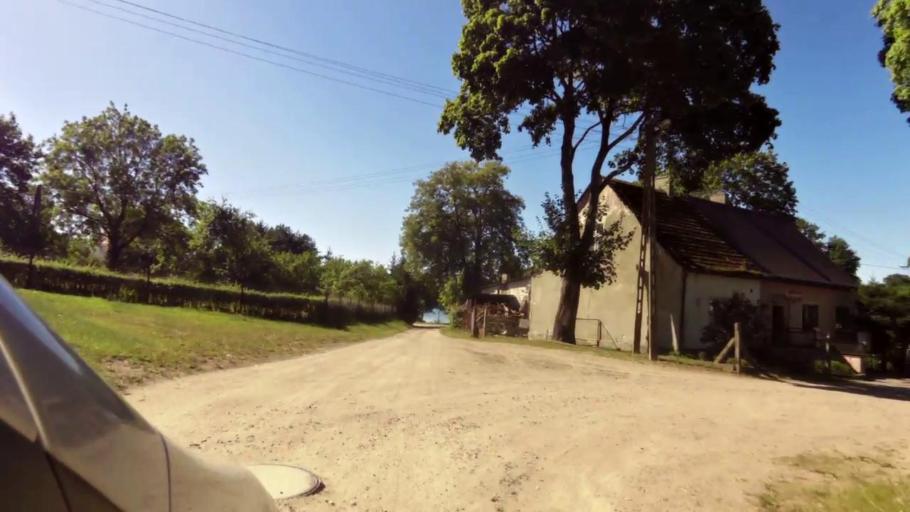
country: PL
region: West Pomeranian Voivodeship
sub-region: Powiat szczecinecki
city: Bialy Bor
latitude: 53.8213
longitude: 16.7665
